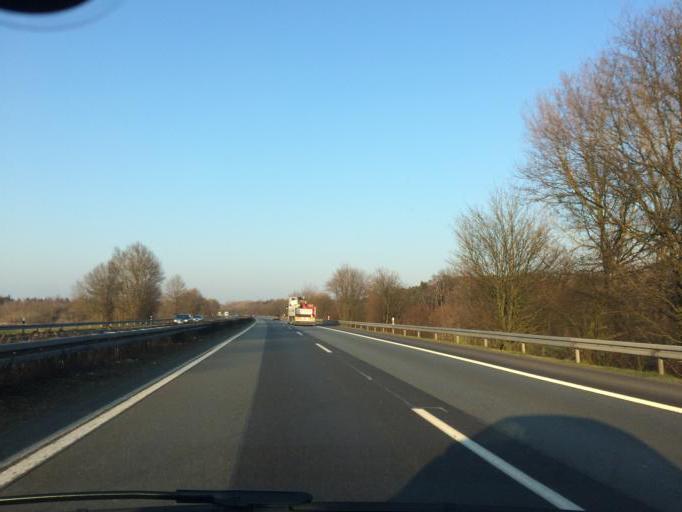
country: DE
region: North Rhine-Westphalia
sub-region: Regierungsbezirk Munster
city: Dulmen
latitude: 51.8229
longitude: 7.2251
